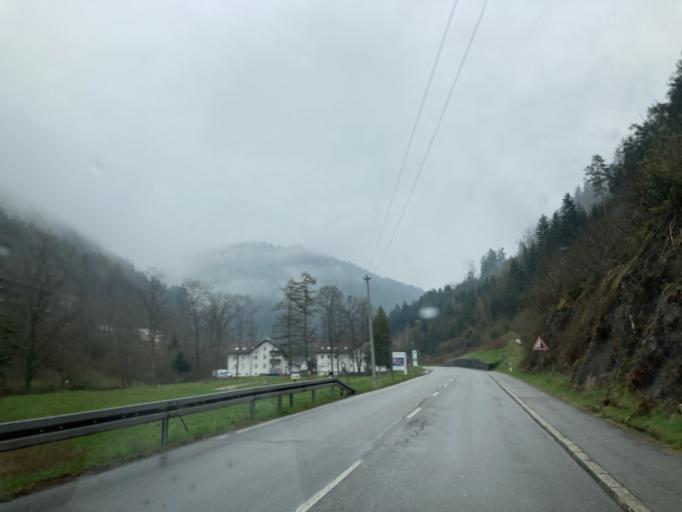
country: DE
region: Baden-Wuerttemberg
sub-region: Freiburg Region
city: Hornberg
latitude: 48.2171
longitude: 8.2422
